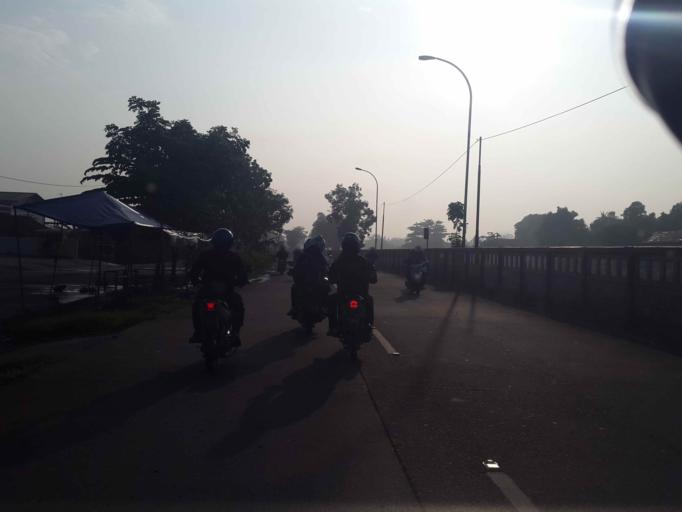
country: ID
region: West Java
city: Cikarang
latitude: -6.2781
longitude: 107.0698
